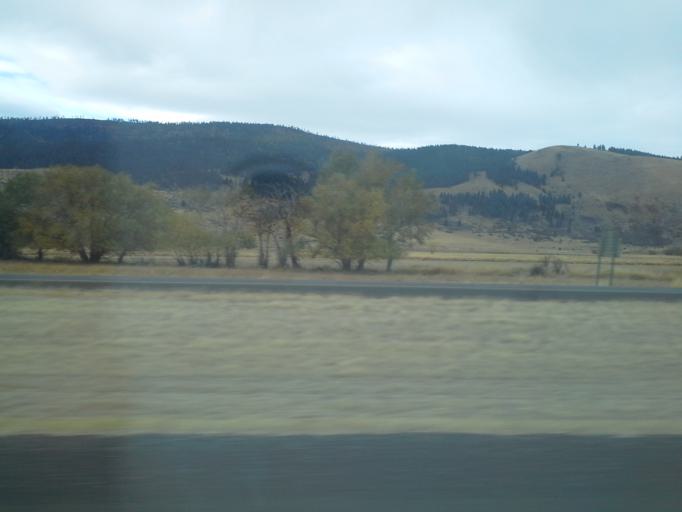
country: US
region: Oregon
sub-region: Union County
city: La Grande
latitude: 45.2603
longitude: -118.0236
